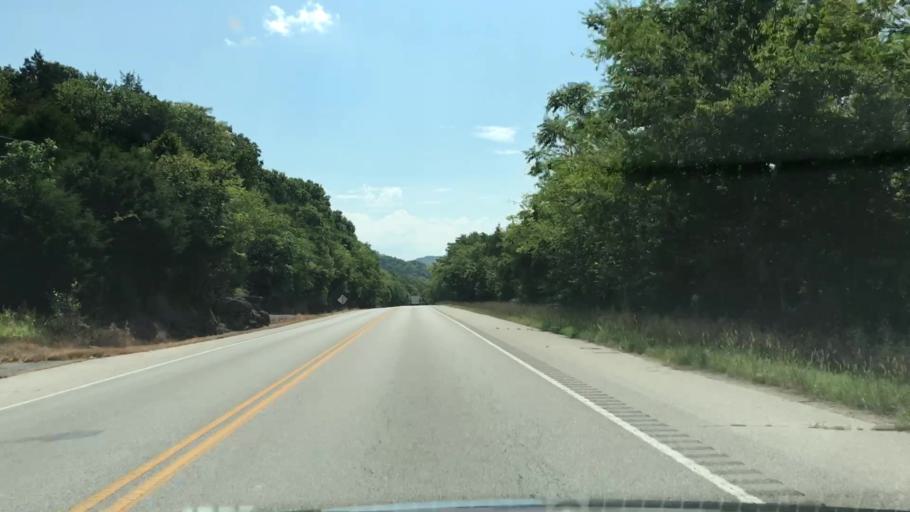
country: US
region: Tennessee
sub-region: Smith County
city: Carthage
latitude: 36.3222
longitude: -86.0171
